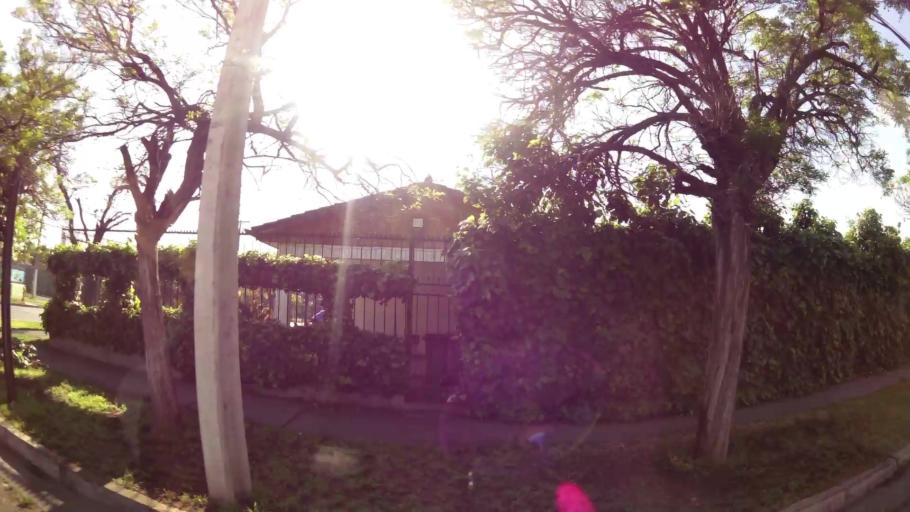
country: CL
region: Santiago Metropolitan
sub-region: Provincia de Santiago
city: La Pintana
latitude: -33.5628
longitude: -70.5885
